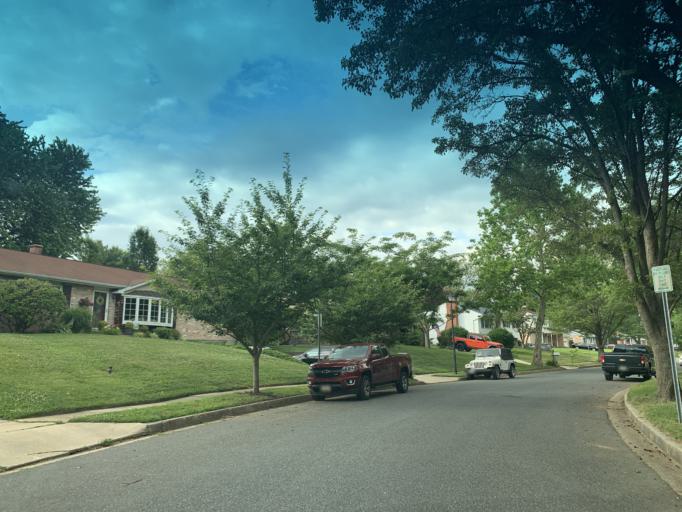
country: US
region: Maryland
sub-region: Harford County
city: South Bel Air
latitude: 39.5304
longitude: -76.3332
